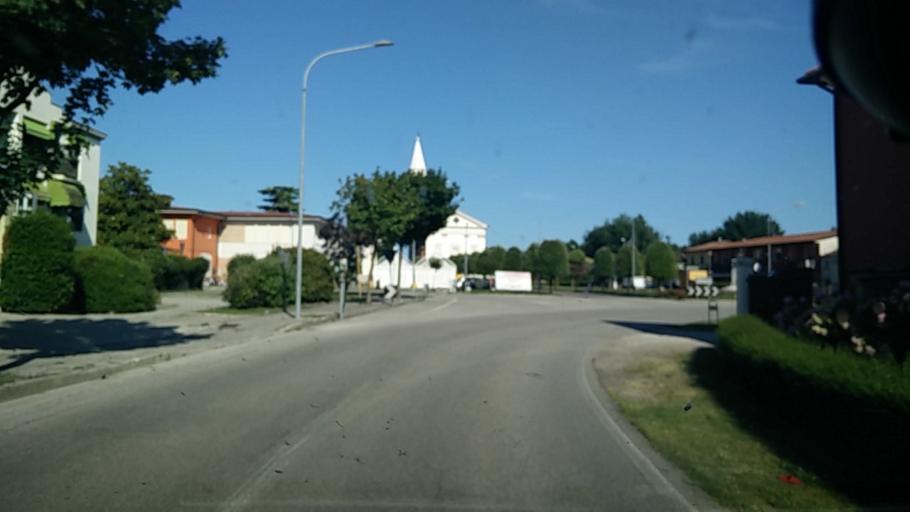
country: IT
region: Veneto
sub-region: Provincia di Treviso
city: Monastier di Treviso
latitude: 45.6786
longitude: 12.4033
